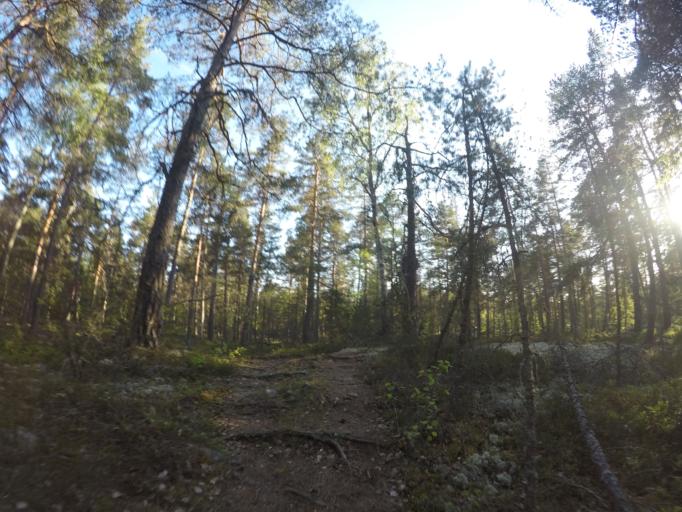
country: SE
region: Soedermanland
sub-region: Eskilstuna Kommun
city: Eskilstuna
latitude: 59.3366
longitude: 16.5230
